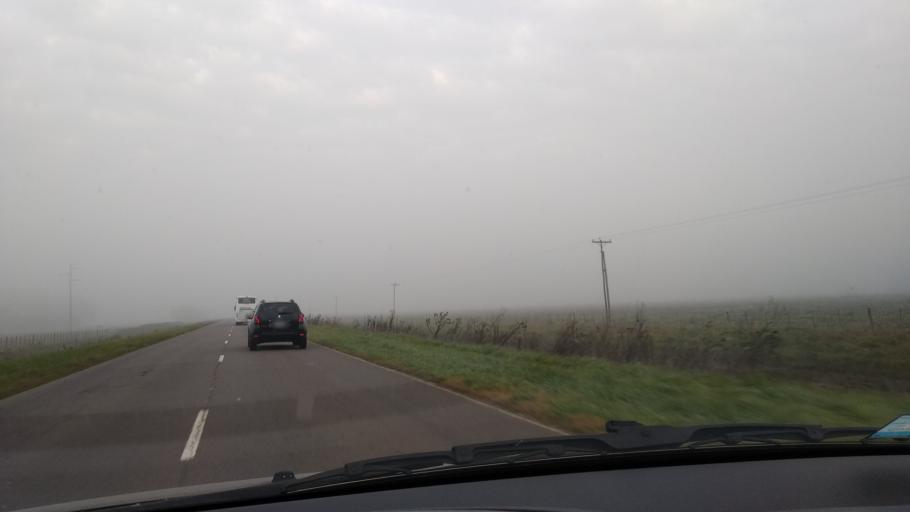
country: AR
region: Buenos Aires
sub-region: Partido de San Vicente
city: San Vicente
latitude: -35.2770
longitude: -58.5500
